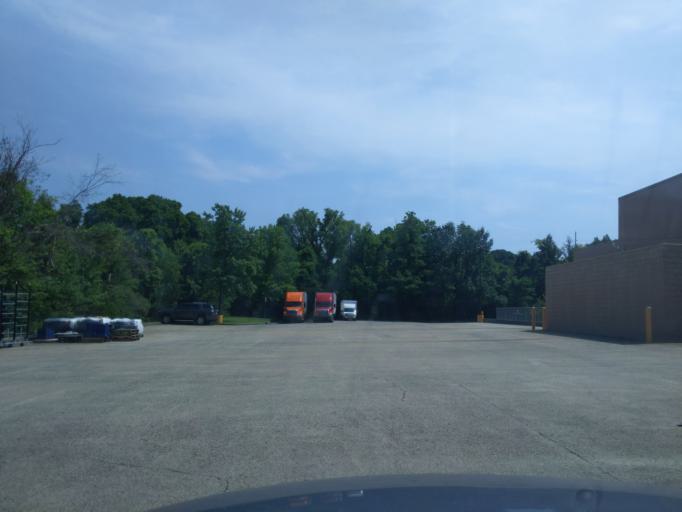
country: US
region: Tennessee
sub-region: Williamson County
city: Brentwood Estates
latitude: 36.0423
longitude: -86.7462
